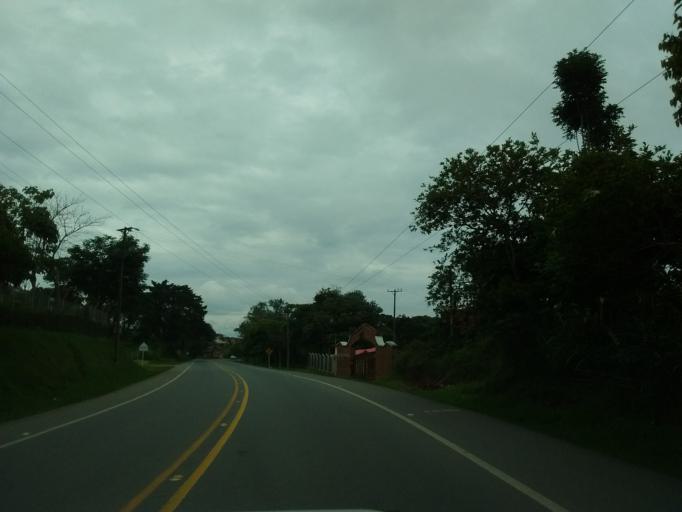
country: CO
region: Cauca
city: Cajibio
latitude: 2.5445
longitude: -76.5589
